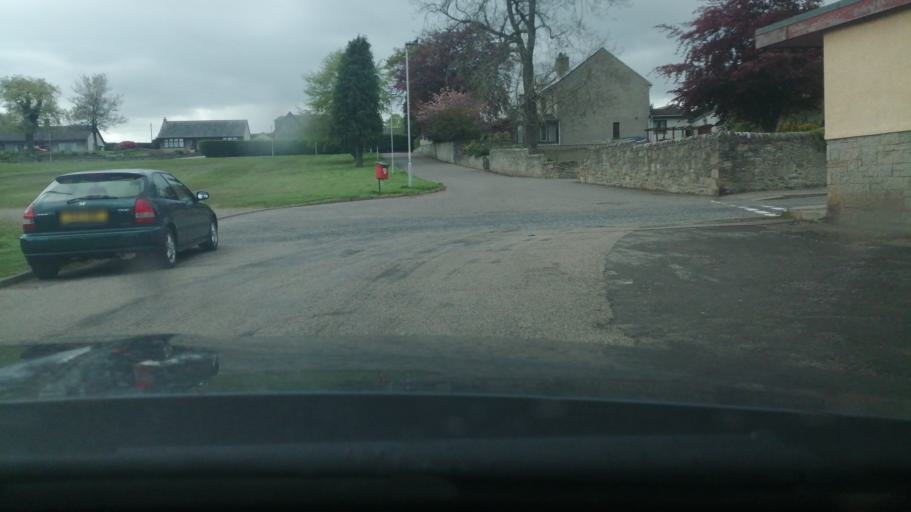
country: GB
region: Scotland
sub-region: Moray
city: Keith
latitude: 57.5361
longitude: -2.9506
